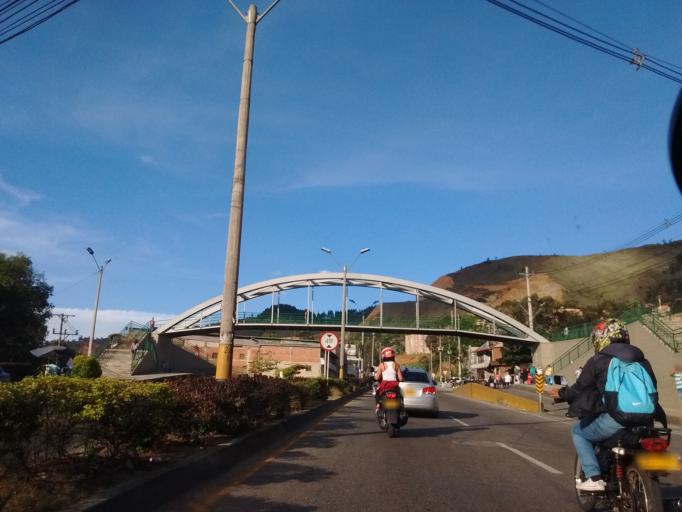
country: CO
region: Antioquia
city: Bello
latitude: 6.3097
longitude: -75.5547
